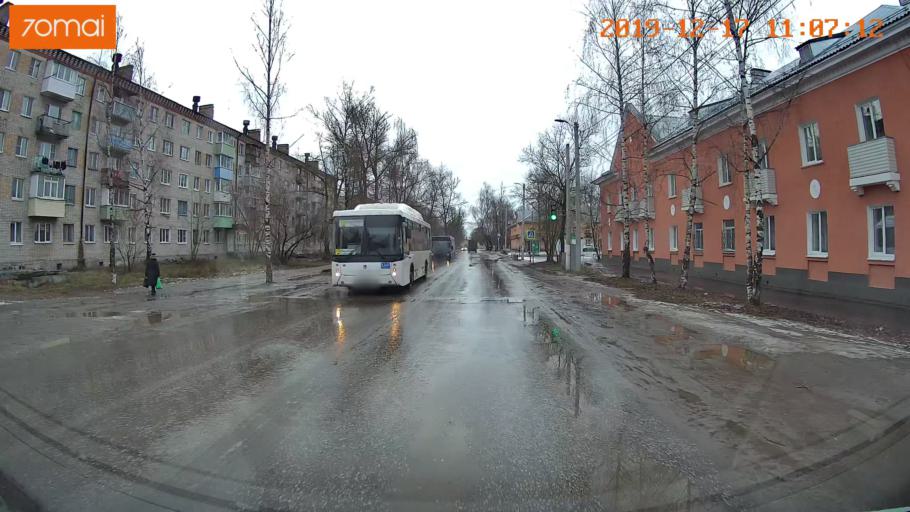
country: RU
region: Vladimir
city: Gus'-Khrustal'nyy
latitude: 55.6120
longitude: 40.6446
